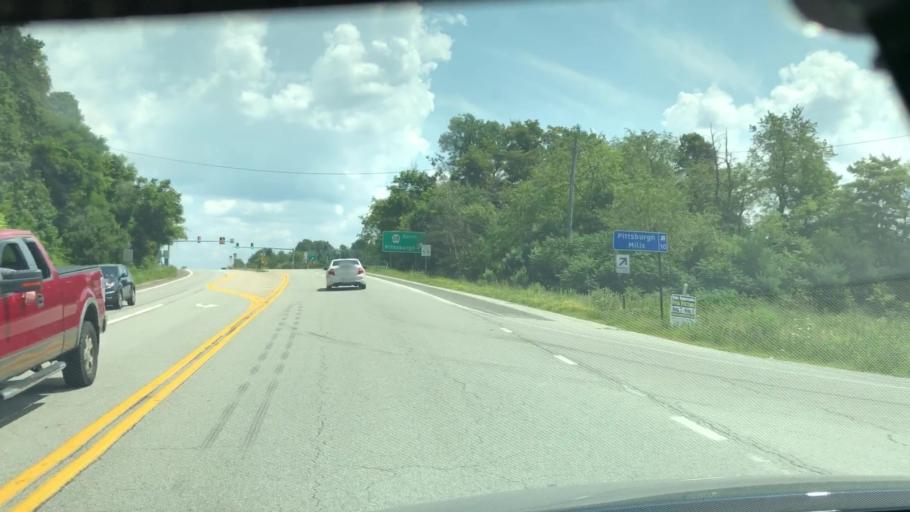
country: US
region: Pennsylvania
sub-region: Armstrong County
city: Freeport
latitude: 40.6925
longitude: -79.7135
